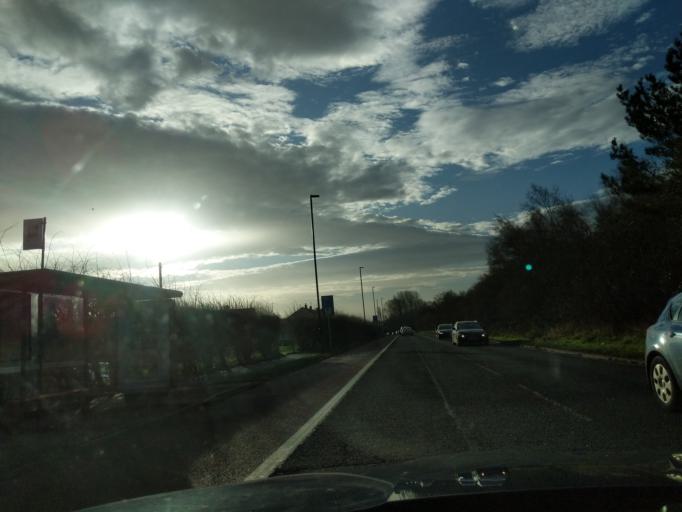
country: GB
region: England
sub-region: Newcastle upon Tyne
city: Gosforth
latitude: 55.0149
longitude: -1.5999
